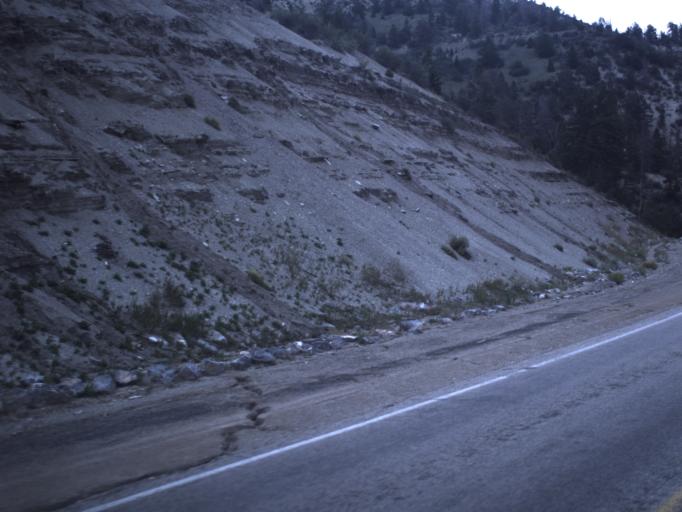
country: US
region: Utah
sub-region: Carbon County
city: Helper
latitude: 39.9015
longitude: -110.7389
